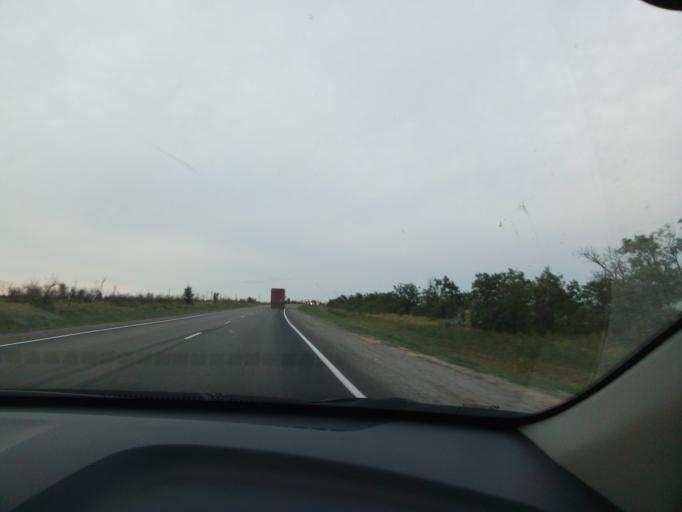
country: RU
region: Volgograd
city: Dubovka
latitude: 49.1464
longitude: 44.8313
